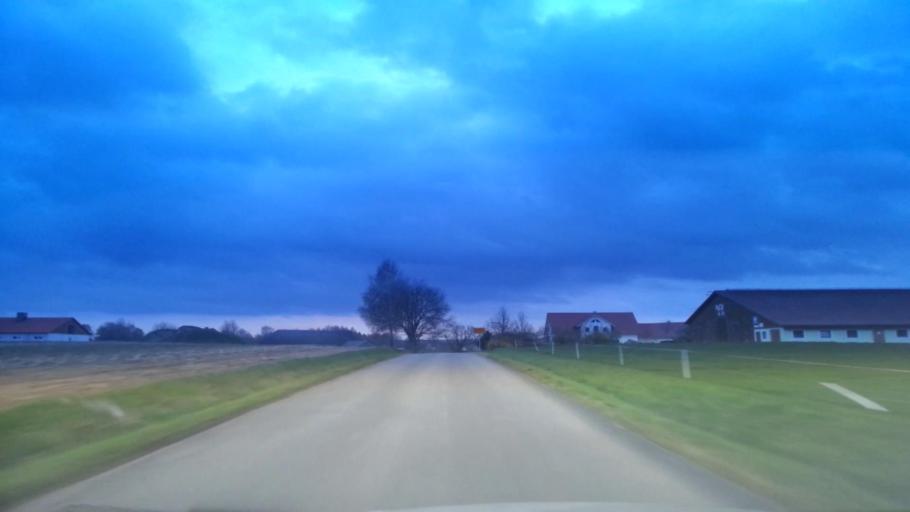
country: DE
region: Bavaria
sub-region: Upper Palatinate
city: Wiesau
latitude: 49.9301
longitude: 12.1745
